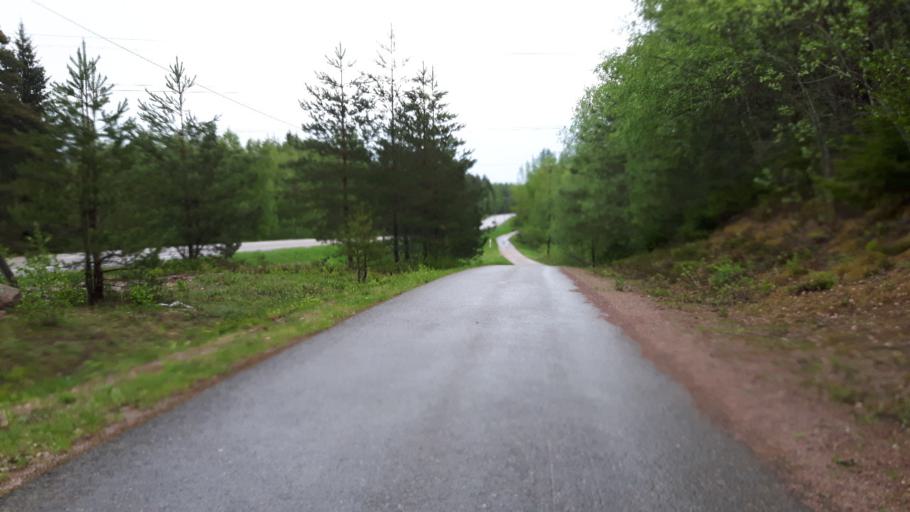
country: FI
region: Kymenlaakso
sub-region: Kotka-Hamina
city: Karhula
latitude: 60.5629
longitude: 27.0613
